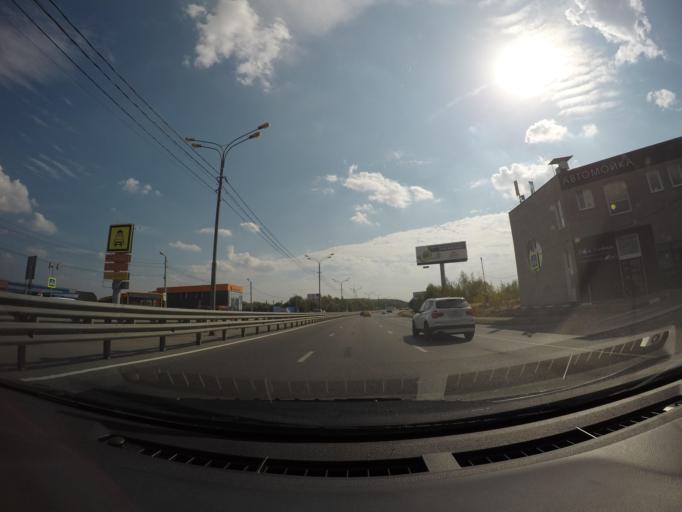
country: RU
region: Moscow
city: Businovo
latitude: 55.9160
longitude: 37.4948
